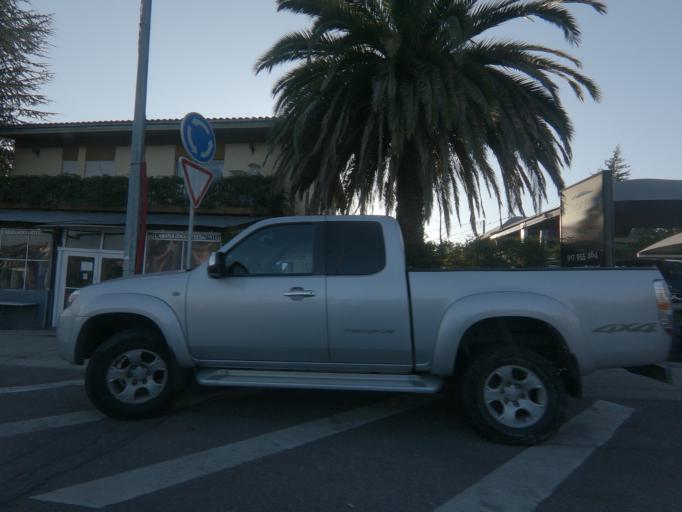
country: PT
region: Vila Real
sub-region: Vila Real
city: Vila Real
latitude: 41.3135
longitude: -7.7338
